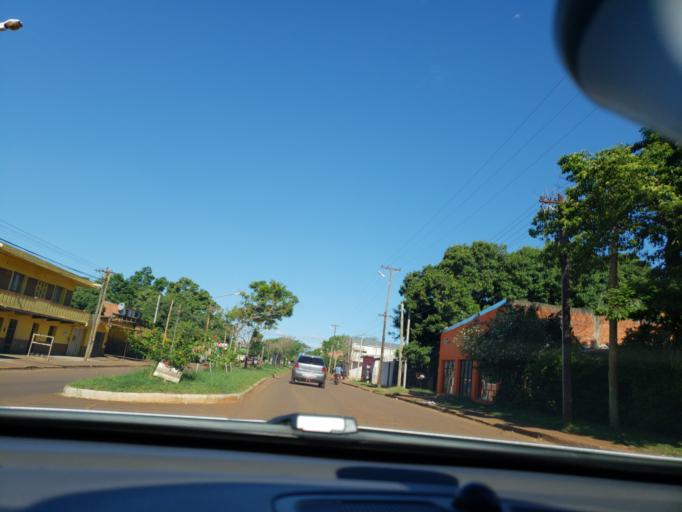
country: AR
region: Misiones
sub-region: Departamento de Capital
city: Posadas
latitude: -27.3844
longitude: -55.9294
